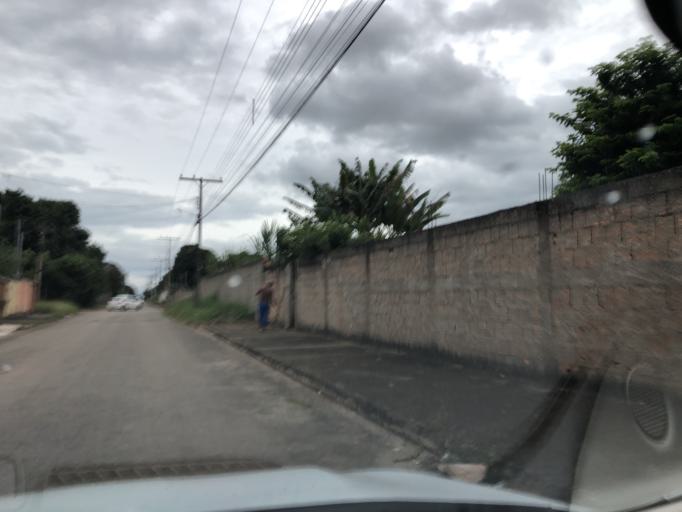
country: BR
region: Goias
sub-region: Luziania
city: Luziania
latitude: -16.1551
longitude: -47.9465
